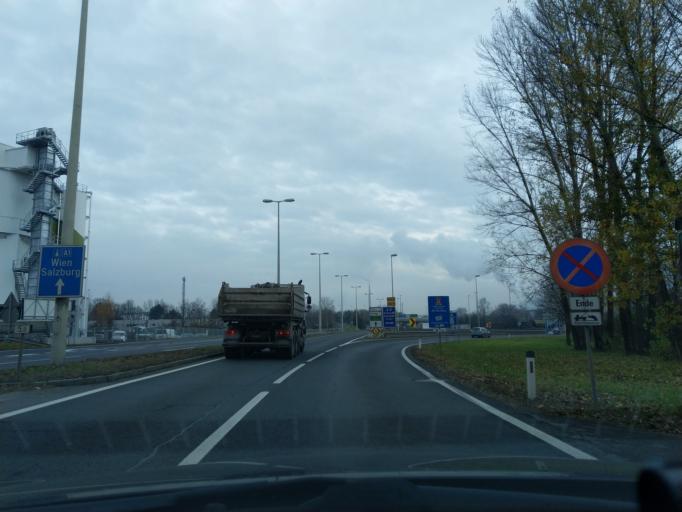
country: AT
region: Upper Austria
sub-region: Linz Stadt
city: Linz
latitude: 48.2822
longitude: 14.3173
